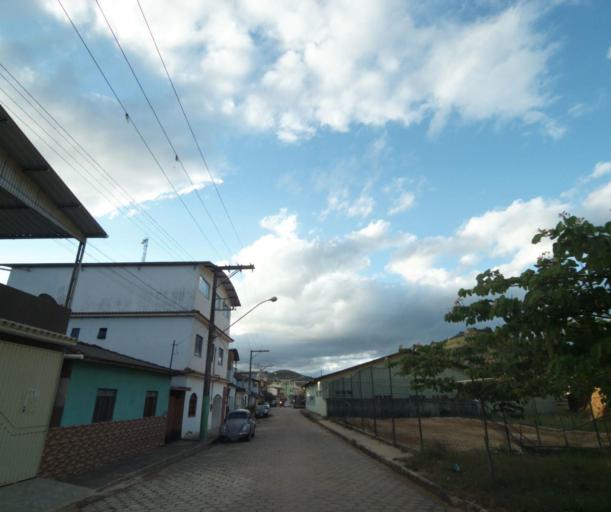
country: BR
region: Espirito Santo
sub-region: Guacui
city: Guacui
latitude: -20.6210
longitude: -41.6833
